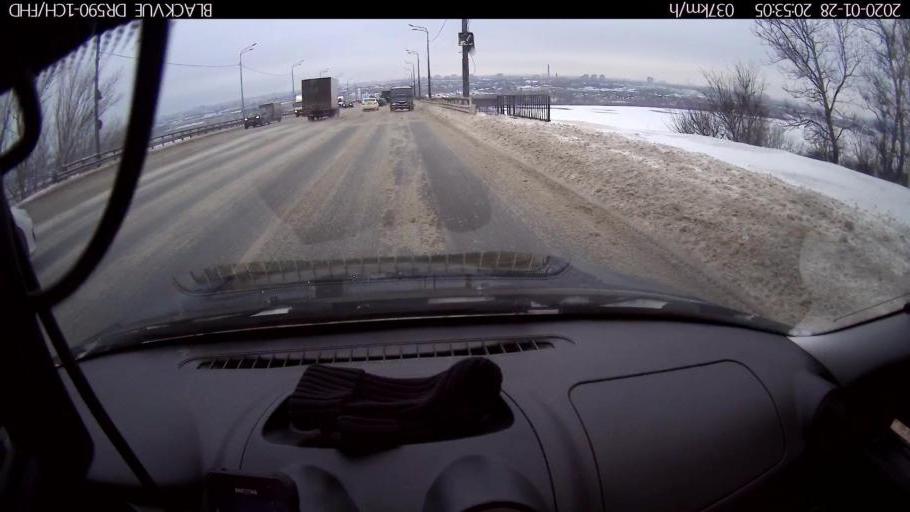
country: RU
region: Nizjnij Novgorod
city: Nizhniy Novgorod
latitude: 56.2473
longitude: 43.9532
